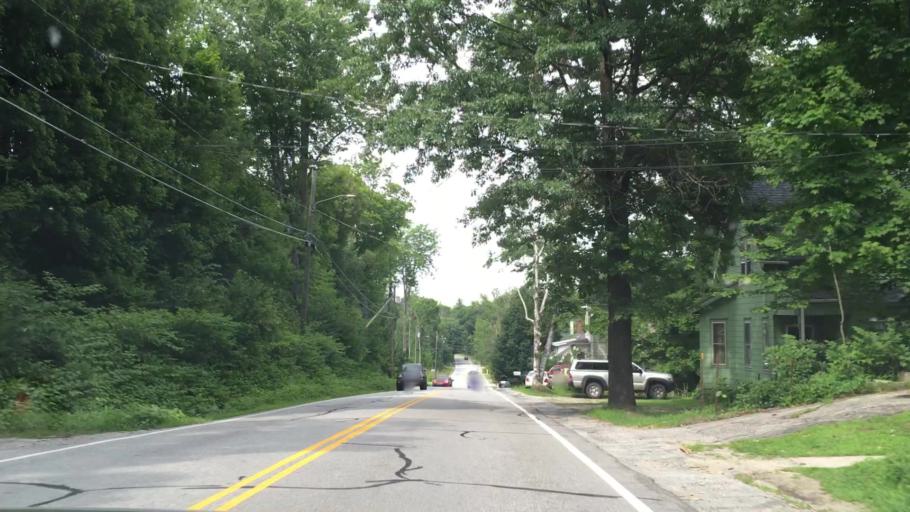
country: US
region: New Hampshire
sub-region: Hillsborough County
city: Antrim
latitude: 43.0323
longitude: -71.9376
